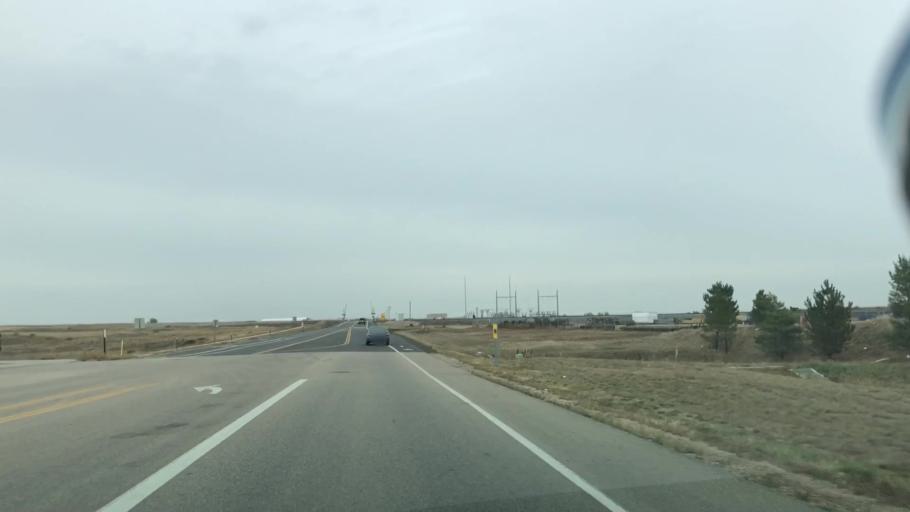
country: US
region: Colorado
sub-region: Larimer County
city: Loveland
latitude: 40.4430
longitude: -105.0204
